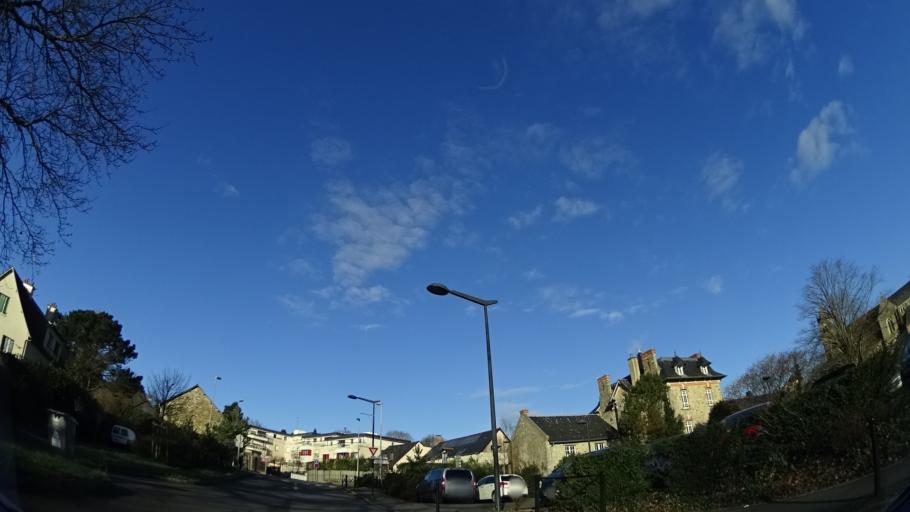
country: FR
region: Brittany
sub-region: Departement d'Ille-et-Vilaine
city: Betton
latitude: 48.1810
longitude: -1.6442
